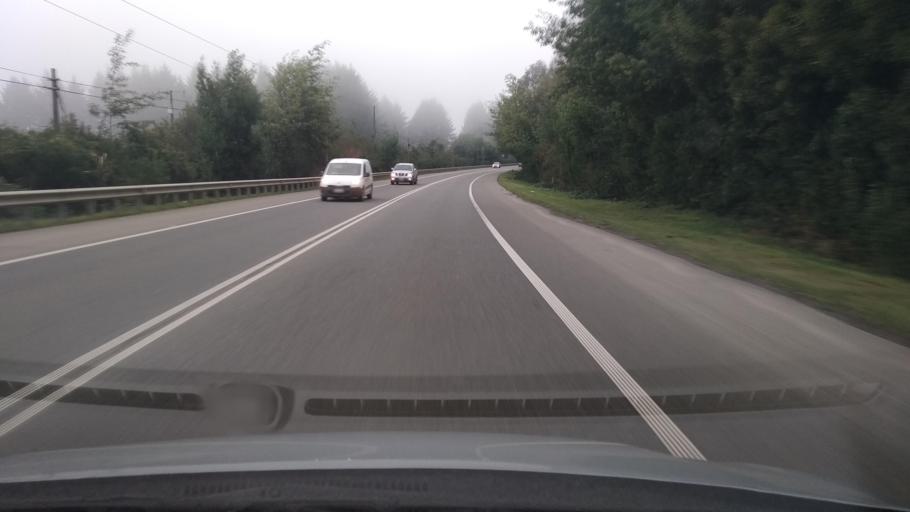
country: CL
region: Los Lagos
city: Las Animas
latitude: -39.7373
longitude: -73.2231
